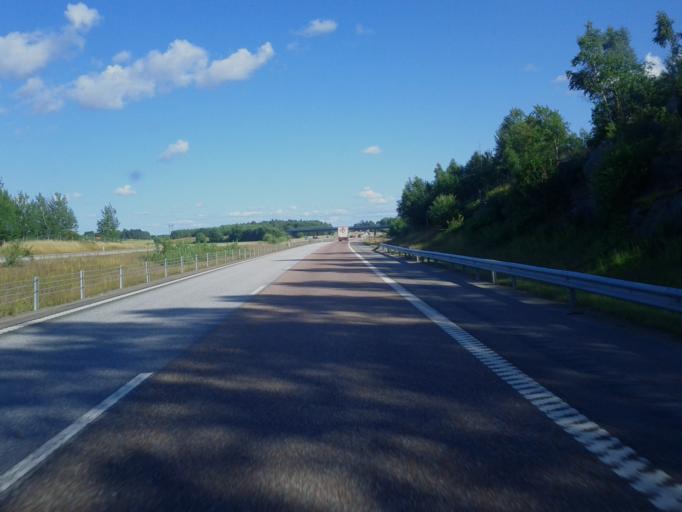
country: SE
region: Uppsala
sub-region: Habo Kommun
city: Balsta
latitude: 59.6058
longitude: 17.4288
